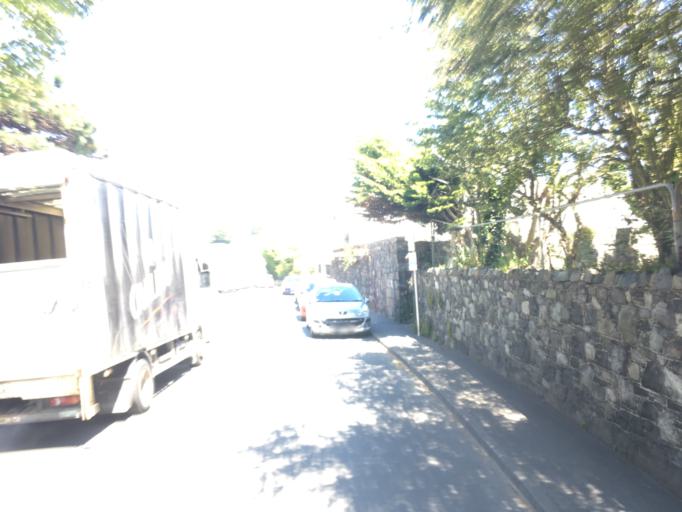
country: GG
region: St Peter Port
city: Saint Peter Port
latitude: 49.4852
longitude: -2.5190
